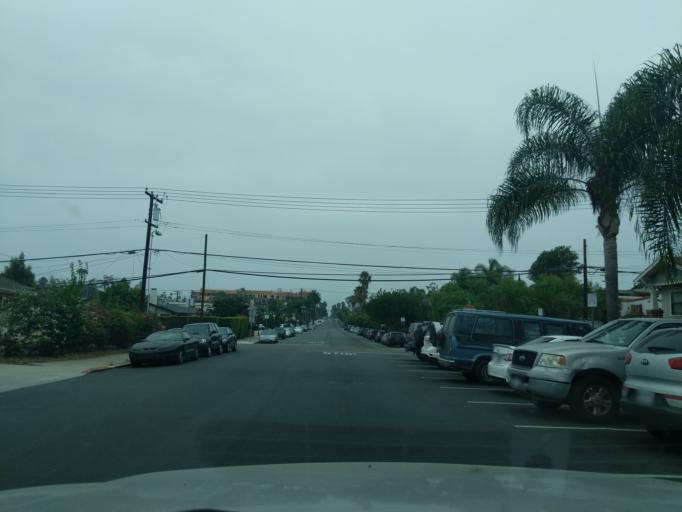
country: US
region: California
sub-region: San Diego County
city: San Diego
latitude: 32.7518
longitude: -117.1425
